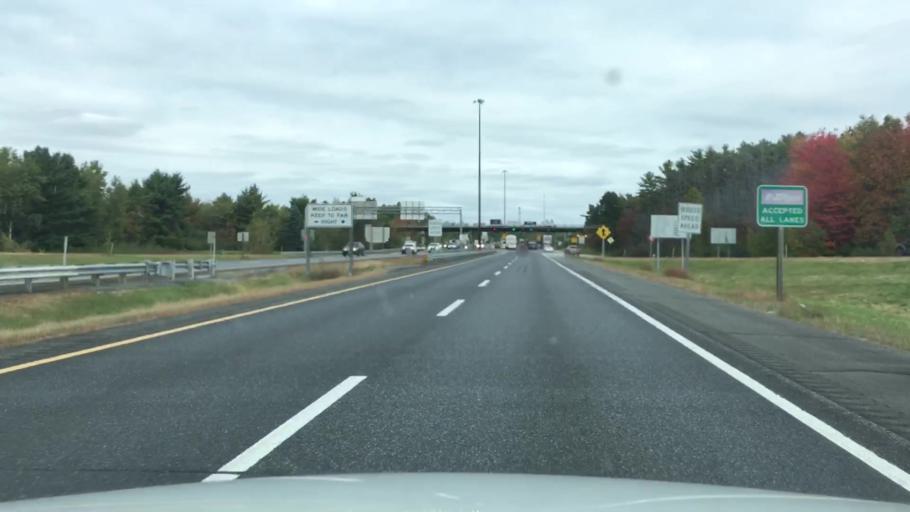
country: US
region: Maine
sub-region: Kennebec County
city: Gardiner
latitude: 44.2103
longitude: -69.8244
